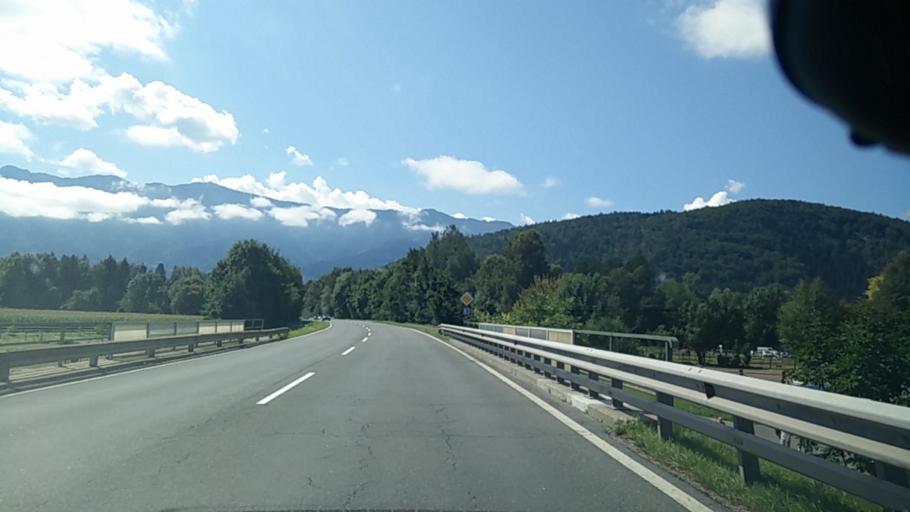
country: AT
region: Carinthia
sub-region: Villach Stadt
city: Villach
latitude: 46.5885
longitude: 13.8333
